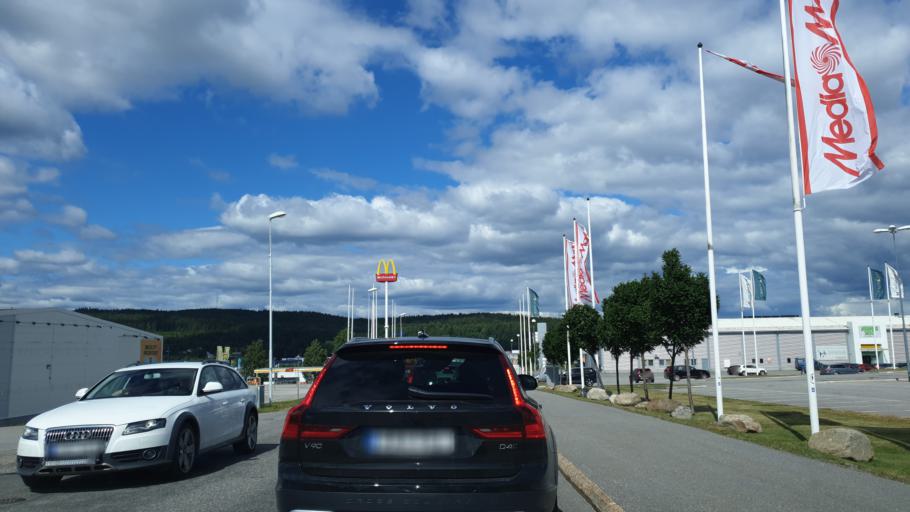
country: SE
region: Vaesternorrland
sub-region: Sundsvalls Kommun
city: Sundsbruk
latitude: 62.4400
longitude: 17.3313
